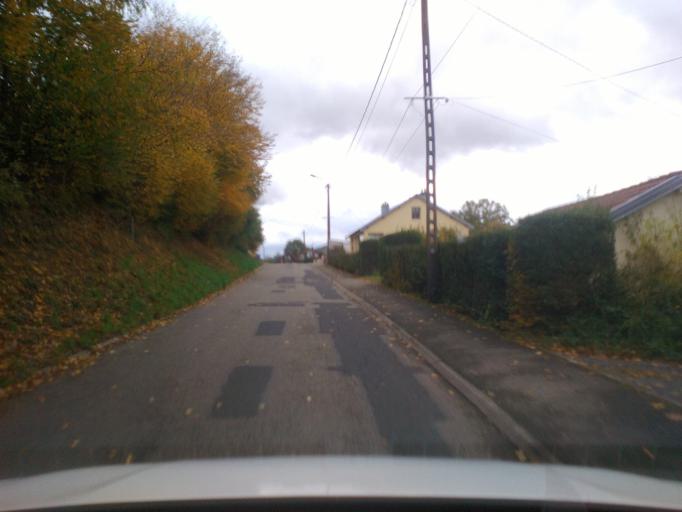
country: FR
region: Lorraine
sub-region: Departement des Vosges
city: Moyenmoutier
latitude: 48.3817
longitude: 6.9257
